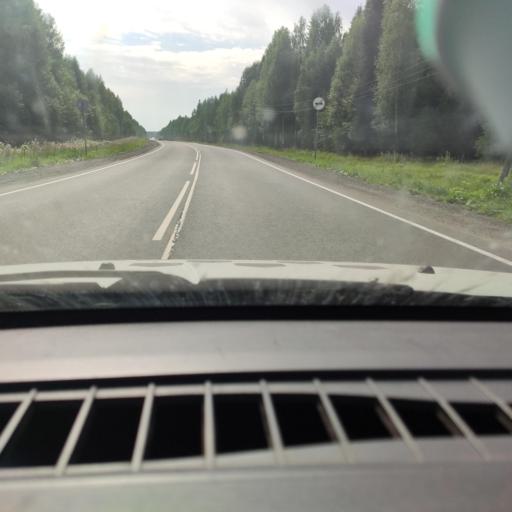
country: RU
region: Kirov
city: Kostino
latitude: 58.8212
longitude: 52.9699
